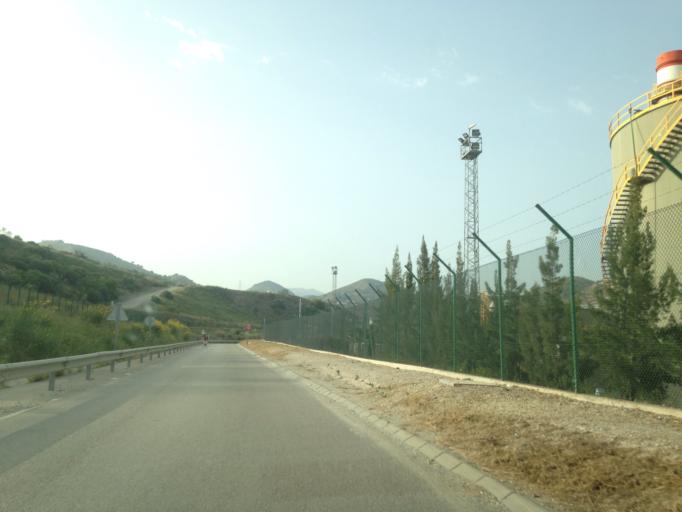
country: ES
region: Andalusia
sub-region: Provincia de Malaga
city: Estacion de Cartama
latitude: 36.7482
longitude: -4.5638
